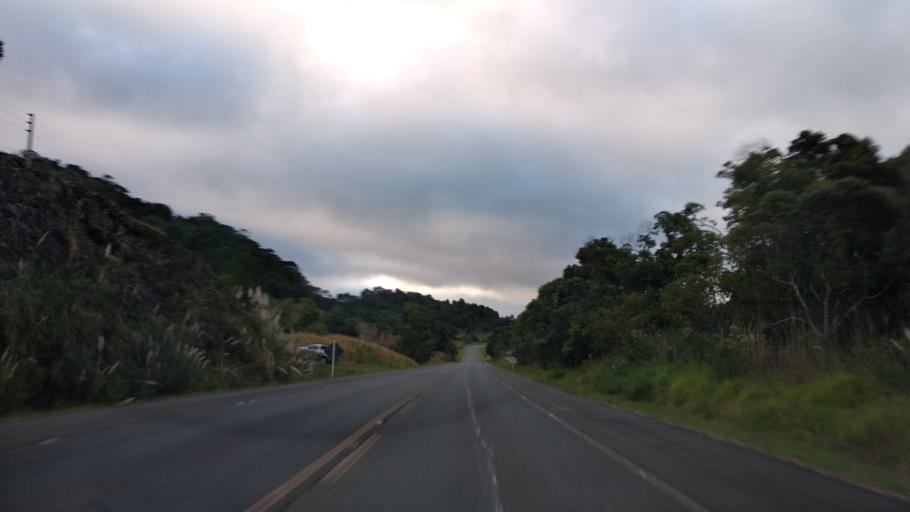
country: BR
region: Santa Catarina
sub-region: Campos Novos
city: Campos Novos
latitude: -27.4963
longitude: -50.9369
